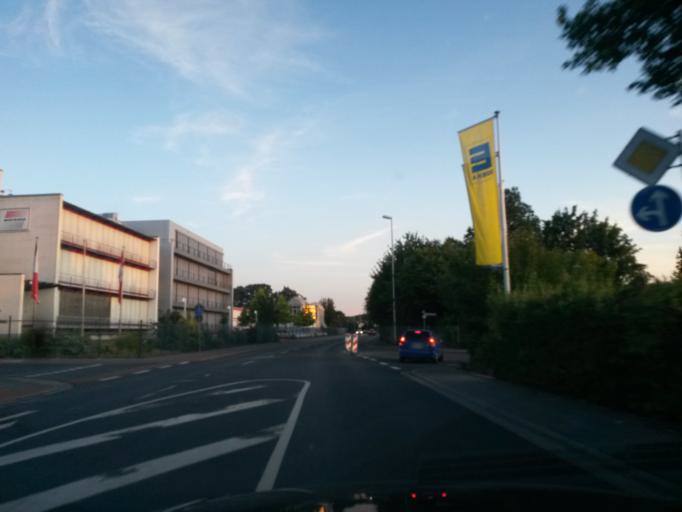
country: DE
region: Bavaria
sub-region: Regierungsbezirk Unterfranken
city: Marktheidenfeld
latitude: 49.8467
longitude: 9.6139
